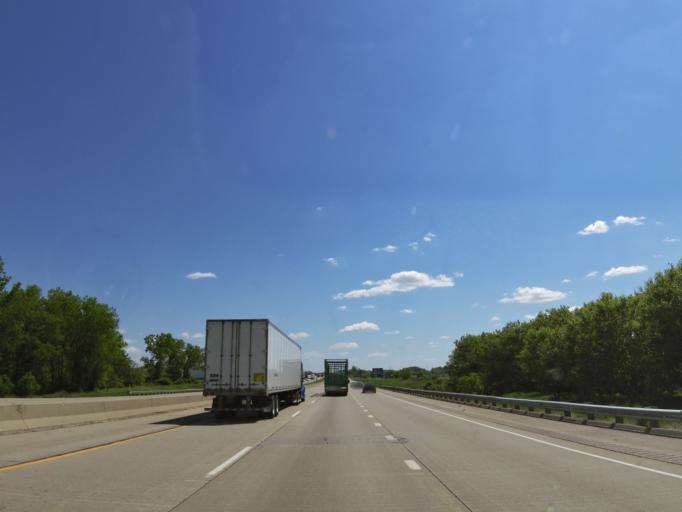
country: US
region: Wisconsin
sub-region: Dane County
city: McFarland
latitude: 43.0613
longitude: -89.2772
